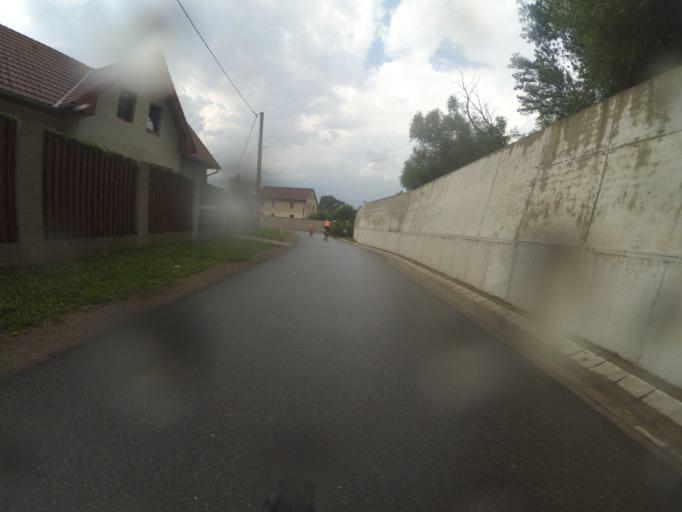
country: CZ
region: Central Bohemia
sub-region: Okres Melnik
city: Melnik
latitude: 50.3427
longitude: 14.4665
